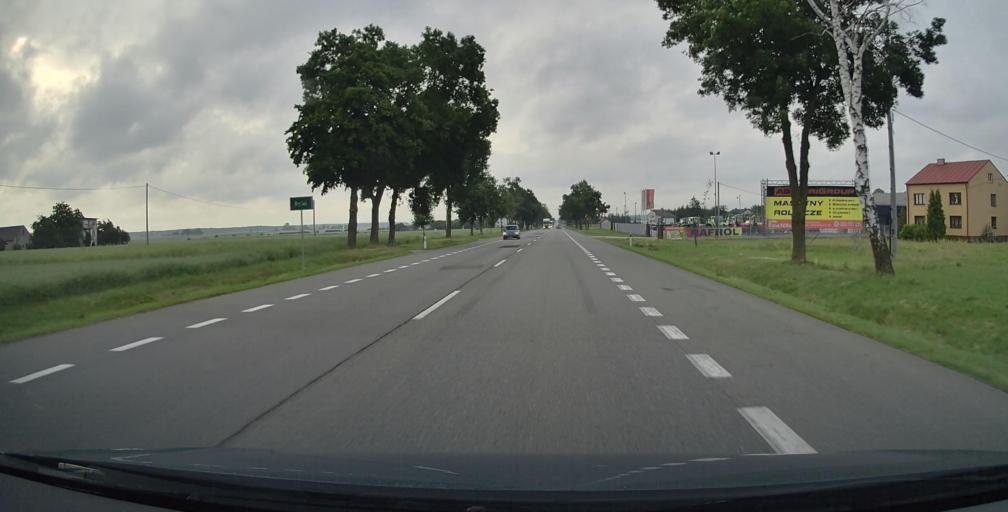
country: PL
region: Masovian Voivodeship
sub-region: Powiat siedlecki
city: Zbuczyn
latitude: 52.1139
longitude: 22.3730
